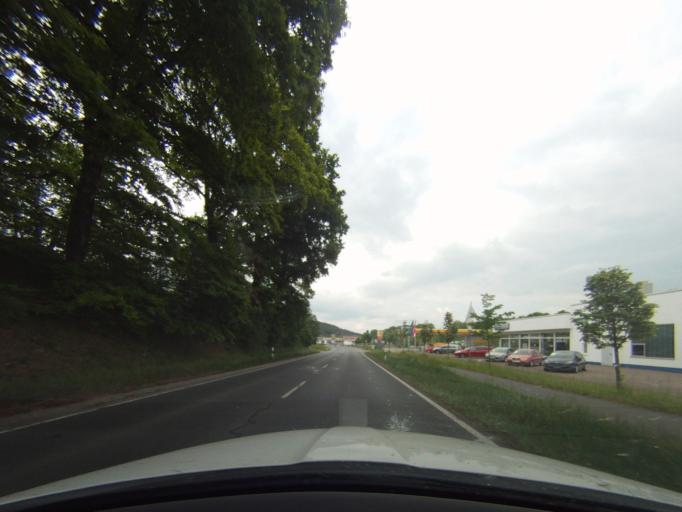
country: DE
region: Thuringia
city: Konigsee
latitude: 50.6670
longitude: 11.1192
